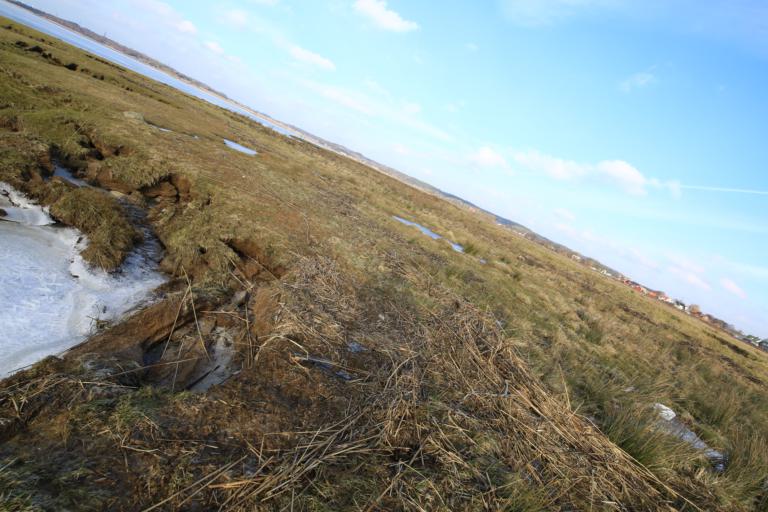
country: SE
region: Halland
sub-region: Kungsbacka Kommun
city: Frillesas
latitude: 57.2148
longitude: 12.2156
